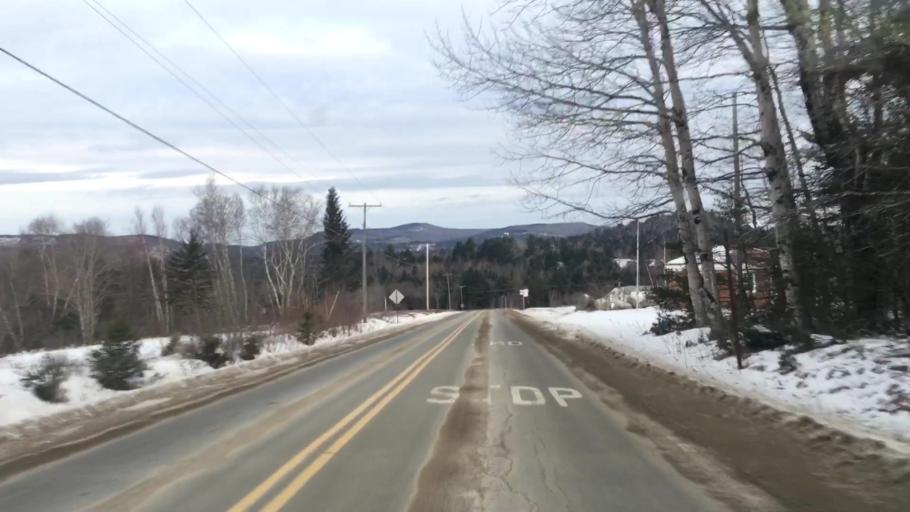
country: US
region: Maine
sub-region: Hancock County
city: Franklin
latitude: 44.8466
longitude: -68.3286
